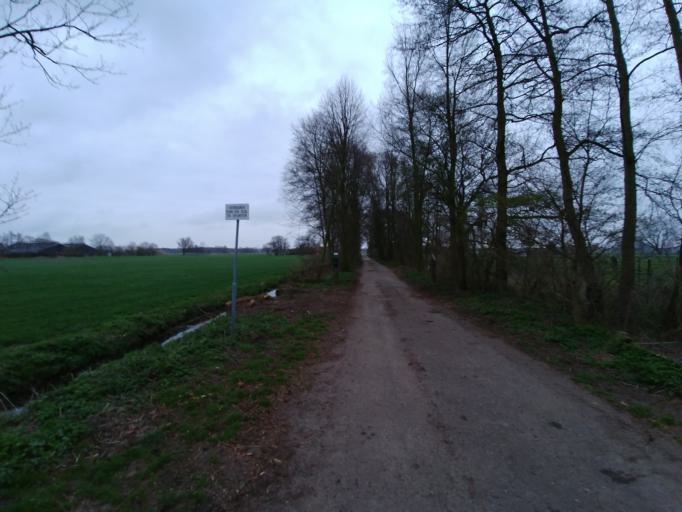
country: NL
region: South Holland
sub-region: Gemeente Leidschendam-Voorburg
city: Voorburg
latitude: 52.1098
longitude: 4.3751
